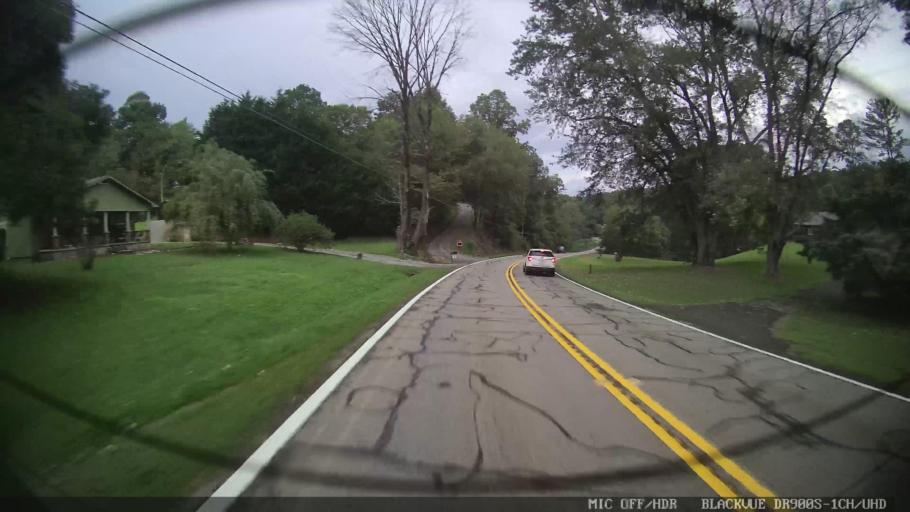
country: US
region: Georgia
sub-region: Gilmer County
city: Ellijay
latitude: 34.7355
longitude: -84.5163
